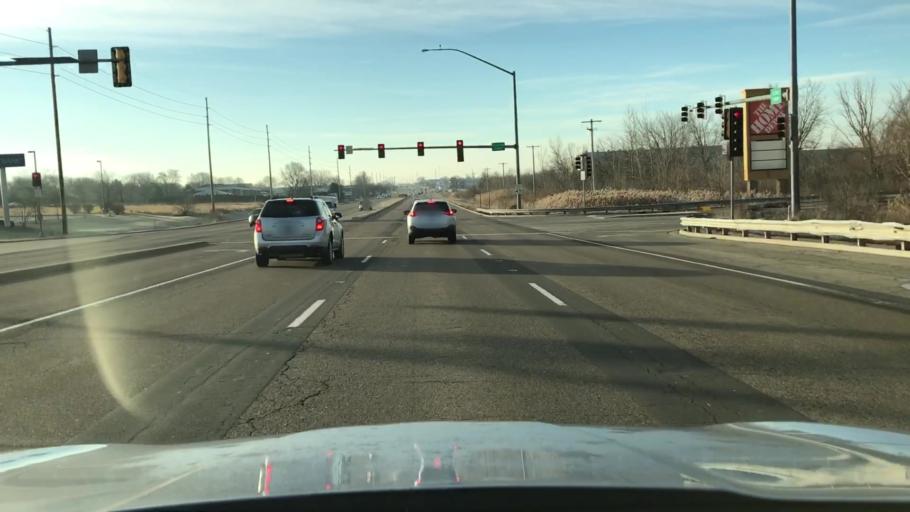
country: US
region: Illinois
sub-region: McLean County
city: Normal
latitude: 40.5252
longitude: -88.9523
